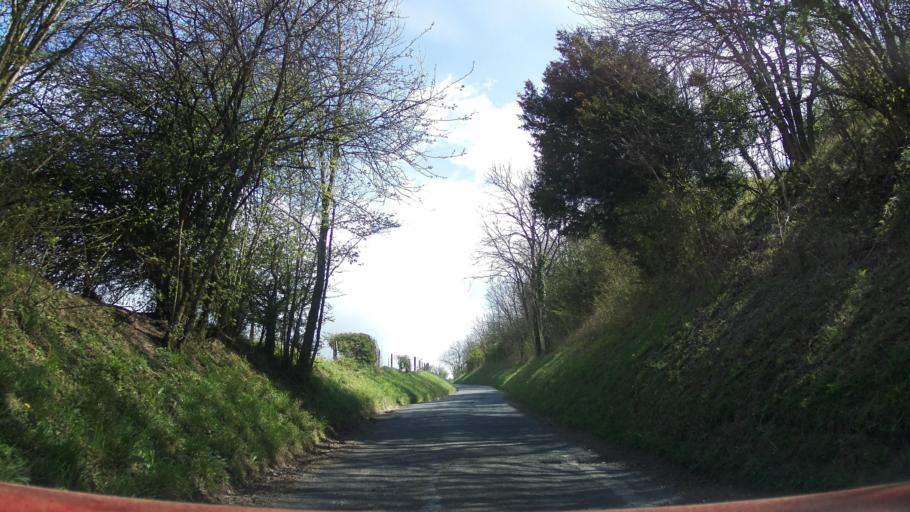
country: GB
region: England
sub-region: West Berkshire
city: Kintbury
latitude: 51.3589
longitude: -1.4738
